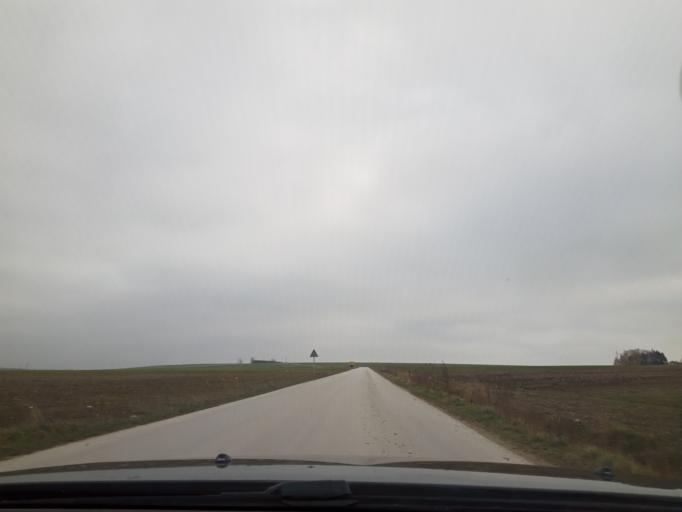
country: PL
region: Swietokrzyskie
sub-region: Powiat jedrzejowski
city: Imielno
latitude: 50.6076
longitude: 20.3960
